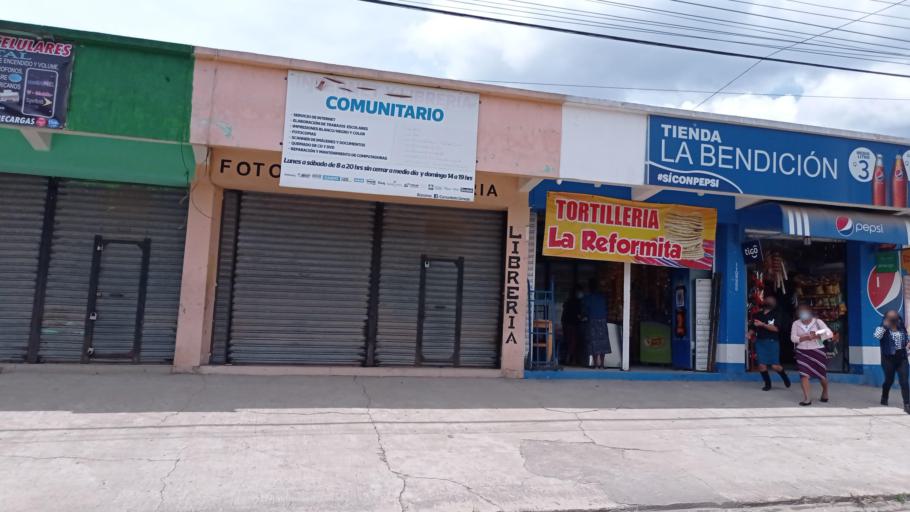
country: GT
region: Quetzaltenango
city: Quetzaltenango
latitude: 14.8494
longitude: -91.5014
